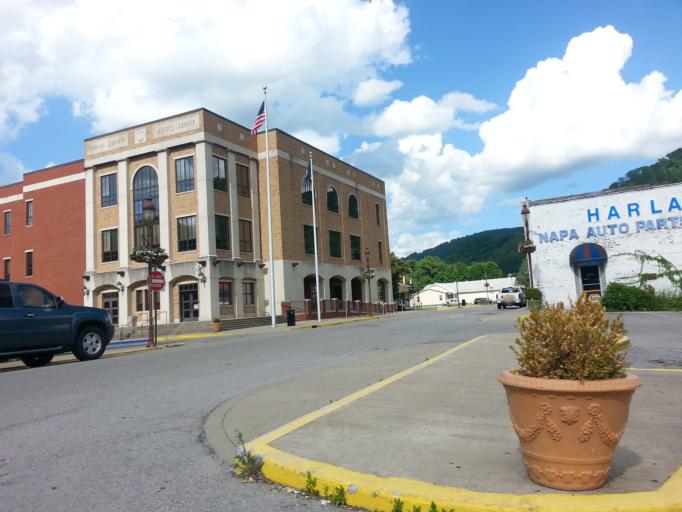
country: US
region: Kentucky
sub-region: Harlan County
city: Harlan
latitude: 36.8458
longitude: -83.3221
